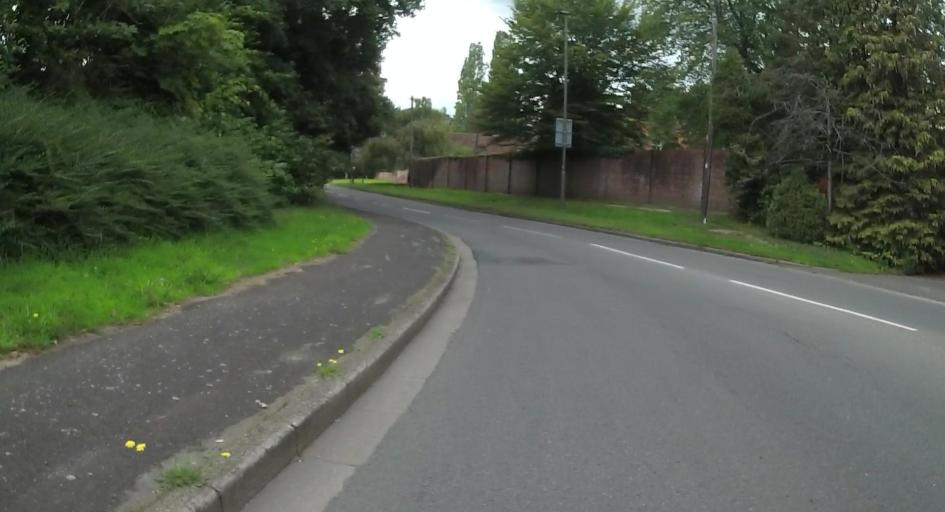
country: GB
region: England
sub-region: Surrey
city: Knaphill
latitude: 51.3243
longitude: -0.6062
